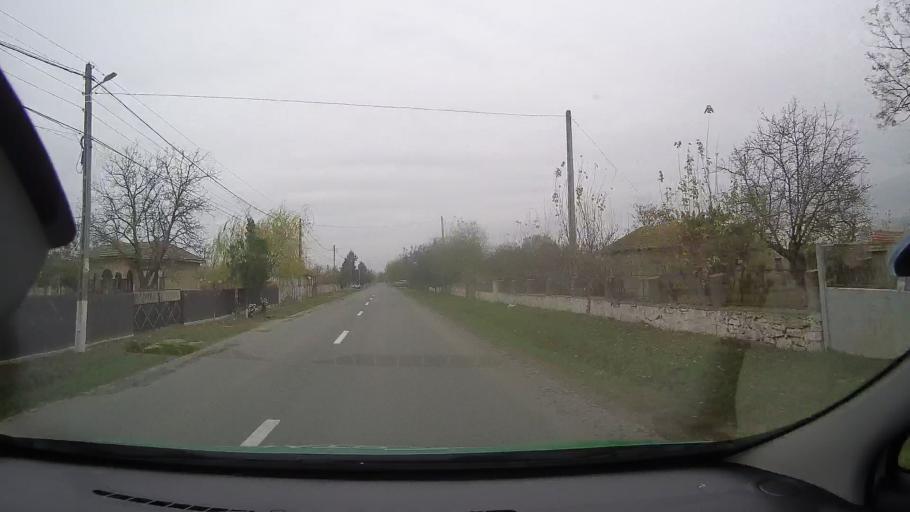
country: RO
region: Constanta
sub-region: Comuna Silistea
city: Silistea
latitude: 44.4430
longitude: 28.2343
